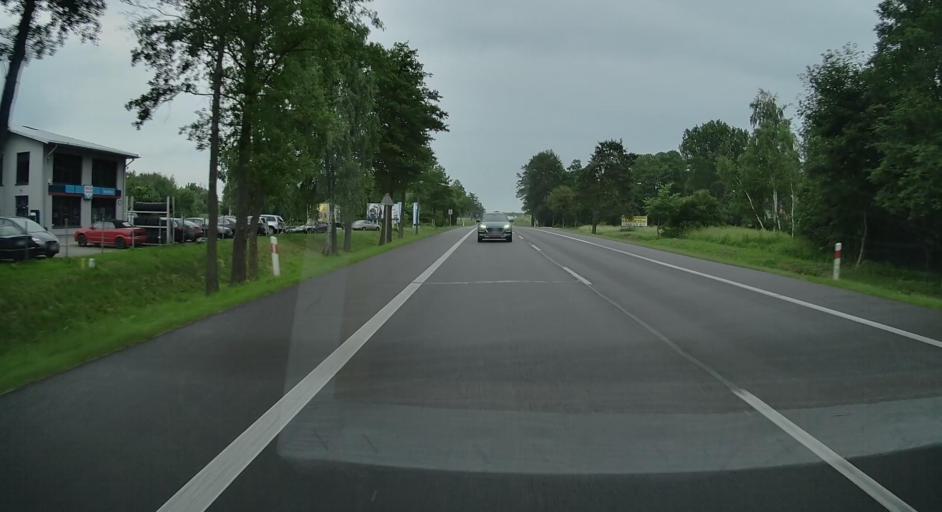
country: PL
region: Lublin Voivodeship
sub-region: Powiat bialski
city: Miedzyrzec Podlaski
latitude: 52.0023
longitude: 22.8196
